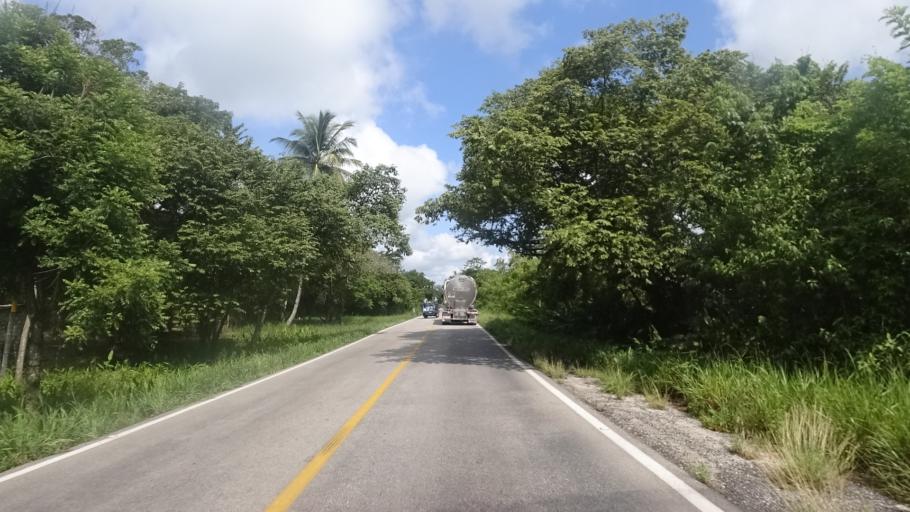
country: MX
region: Chiapas
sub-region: Catazaja
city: Catazaja
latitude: 17.6443
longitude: -92.0309
